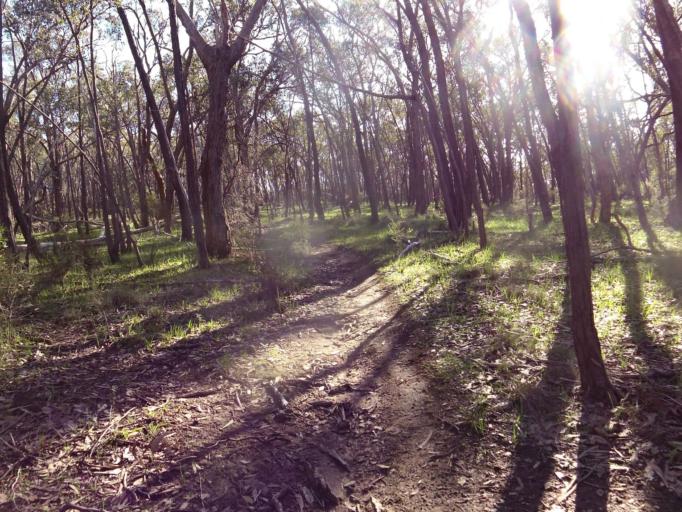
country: AU
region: Victoria
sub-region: Greater Bendigo
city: Kangaroo Flat
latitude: -36.8864
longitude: 144.2859
